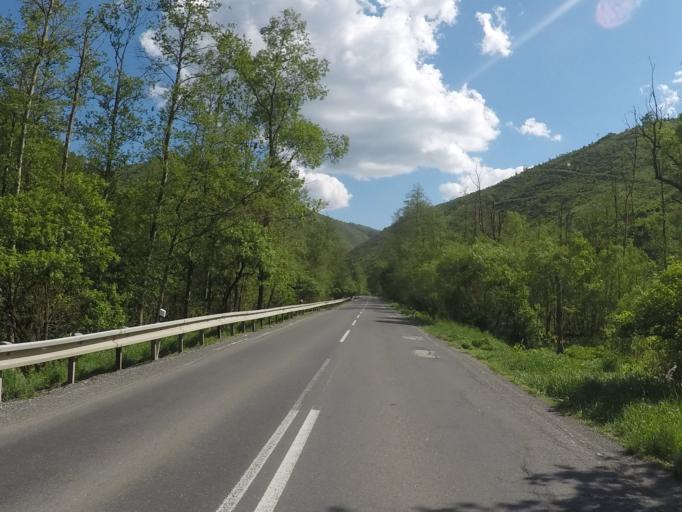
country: SK
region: Presovsky
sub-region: Okres Poprad
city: Poprad
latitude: 48.9622
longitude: 20.2919
